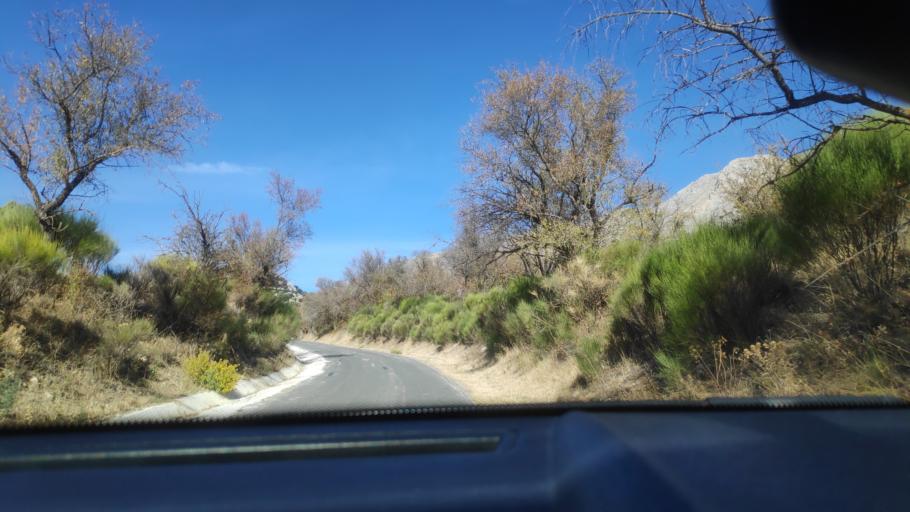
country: ES
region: Andalusia
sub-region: Provincia de Jaen
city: Torres
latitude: 37.7857
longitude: -3.4817
